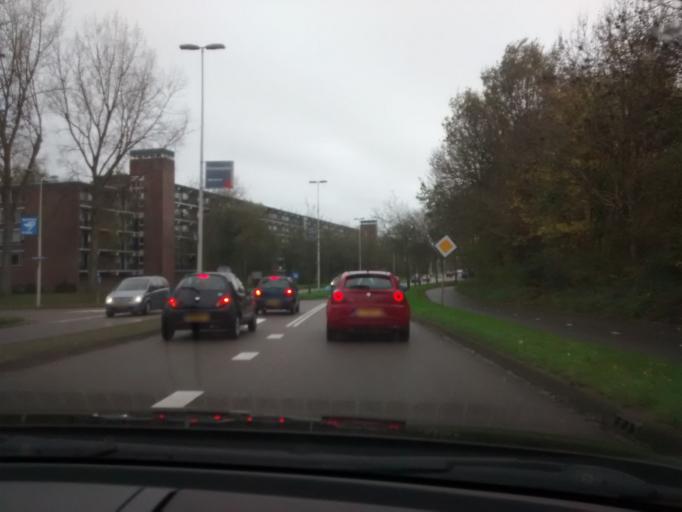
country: NL
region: South Holland
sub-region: Gemeente Oegstgeest
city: Oegstgeest
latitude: 52.1577
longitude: 4.4664
